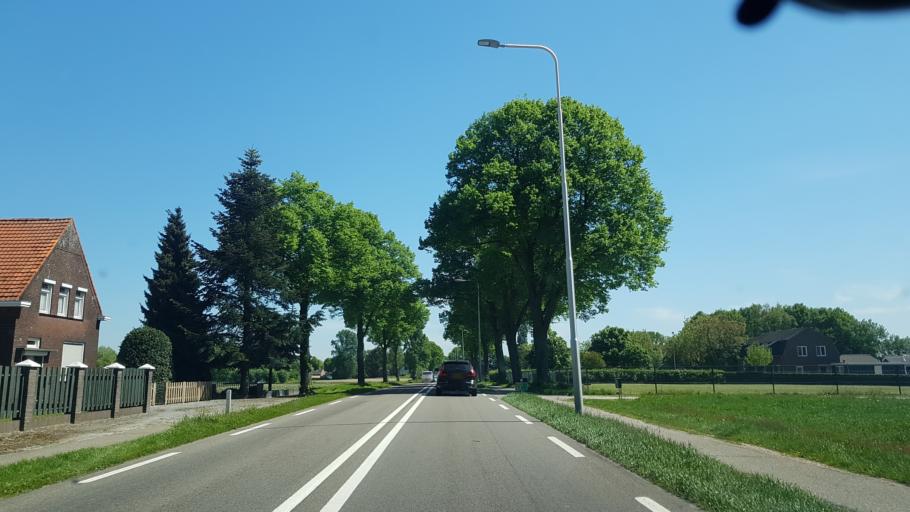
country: NL
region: Limburg
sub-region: Gemeente Leudal
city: Heythuysen
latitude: 51.2244
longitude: 5.8678
